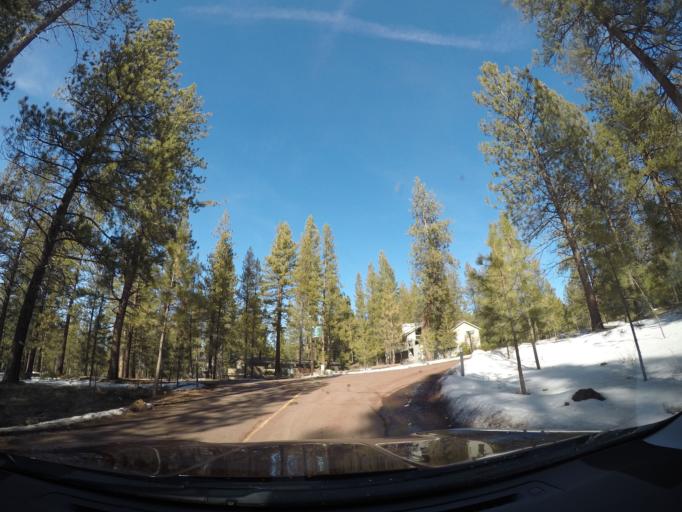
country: US
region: Oregon
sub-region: Deschutes County
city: Sunriver
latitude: 43.8776
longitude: -121.4303
